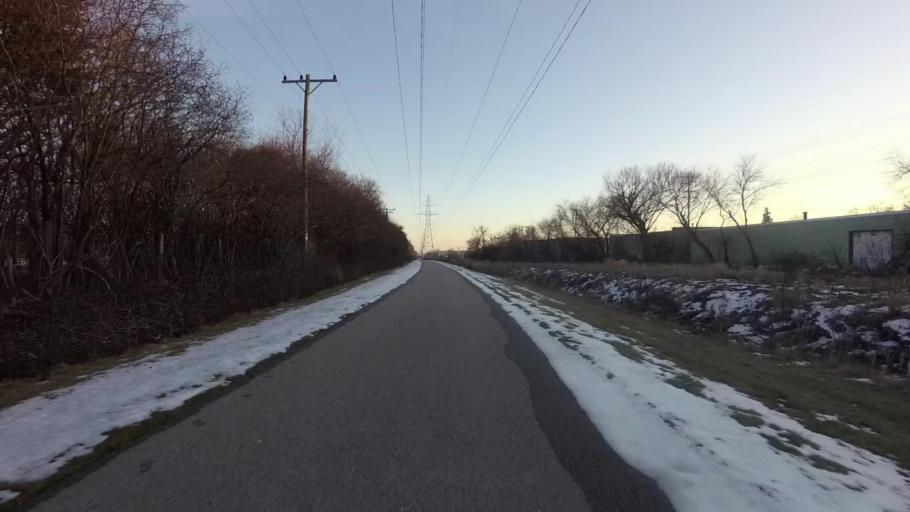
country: US
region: Wisconsin
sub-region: Milwaukee County
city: Brown Deer
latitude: 43.1539
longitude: -87.9568
